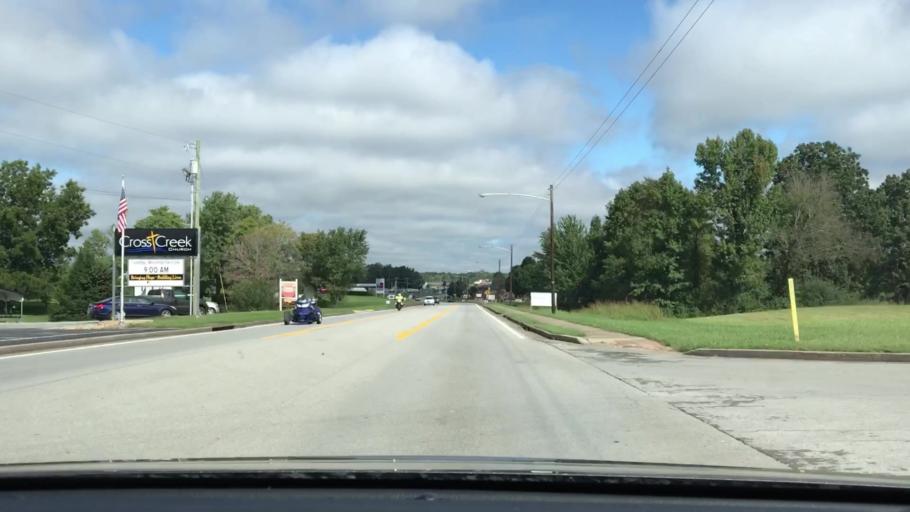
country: US
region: Kentucky
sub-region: Russell County
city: Jamestown
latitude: 37.0065
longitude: -85.0742
